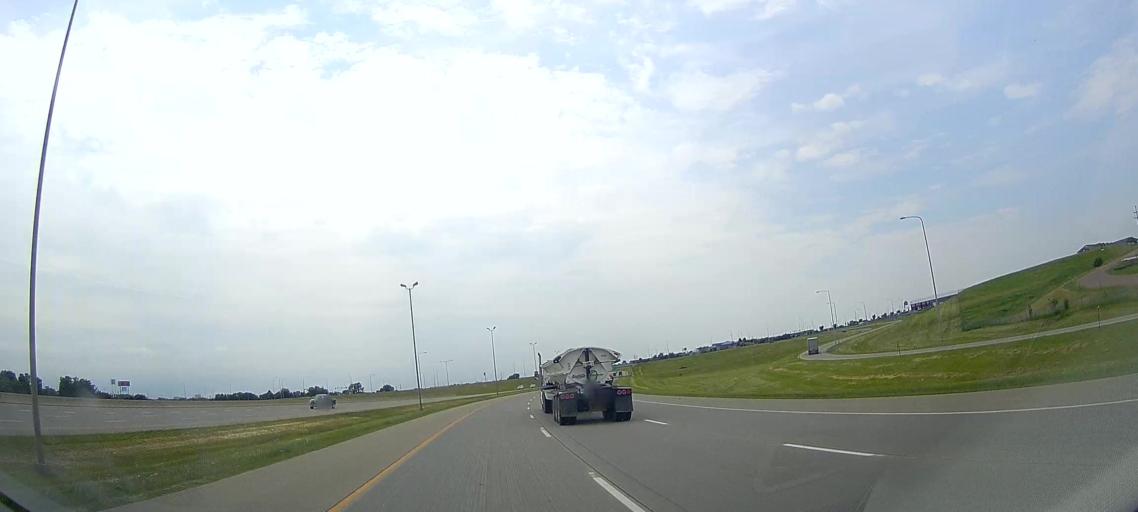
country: US
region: South Dakota
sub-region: Minnehaha County
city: Sioux Falls
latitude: 43.5765
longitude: -96.7718
